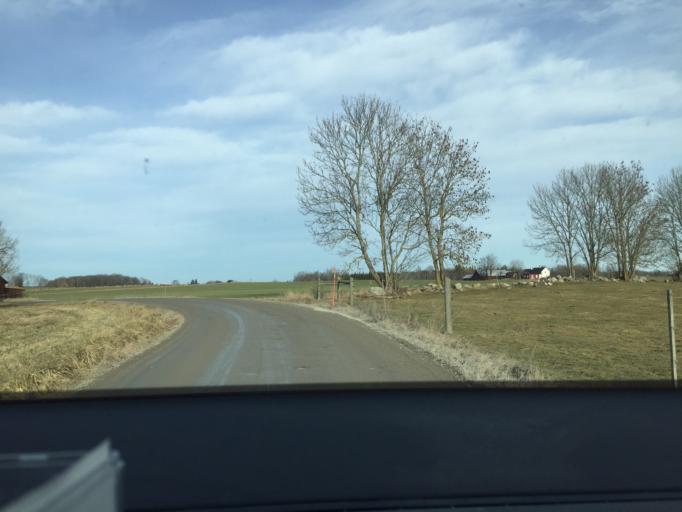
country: SE
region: OErebro
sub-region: Hallsbergs Kommun
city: Skollersta
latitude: 59.1365
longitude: 15.4170
